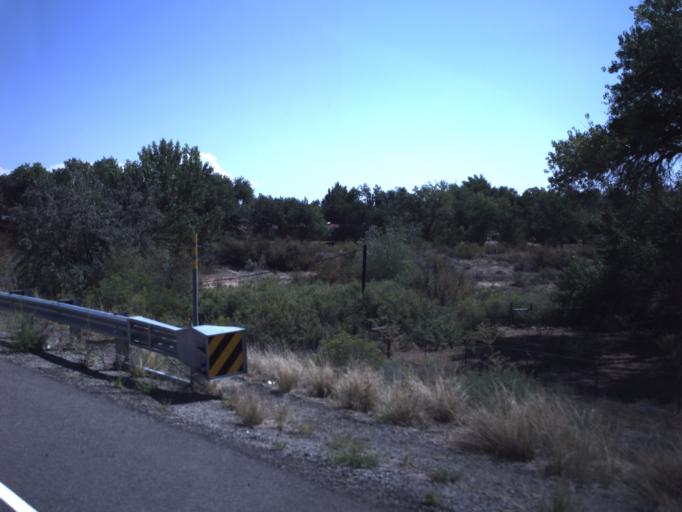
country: US
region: Utah
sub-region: San Juan County
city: Blanding
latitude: 37.2823
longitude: -109.5618
